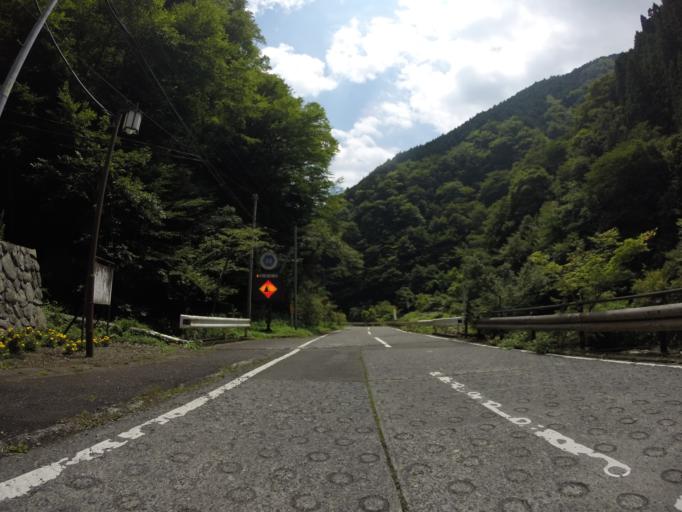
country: JP
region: Shizuoka
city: Fujinomiya
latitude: 35.3044
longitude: 138.3391
